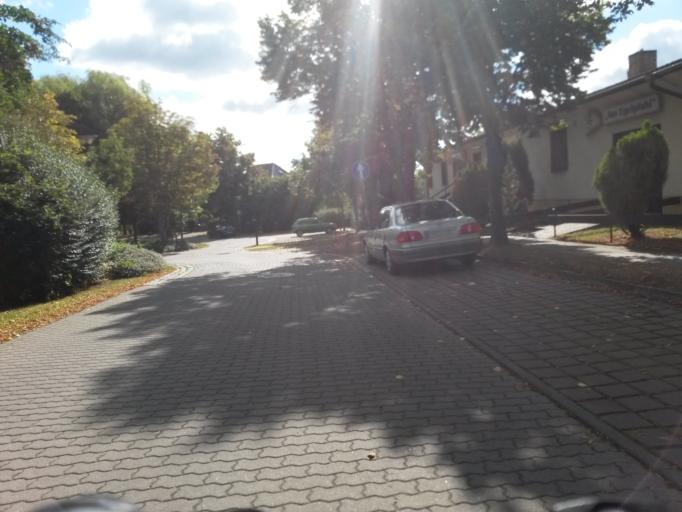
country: DE
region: Brandenburg
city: Templin
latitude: 53.1129
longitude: 13.5033
